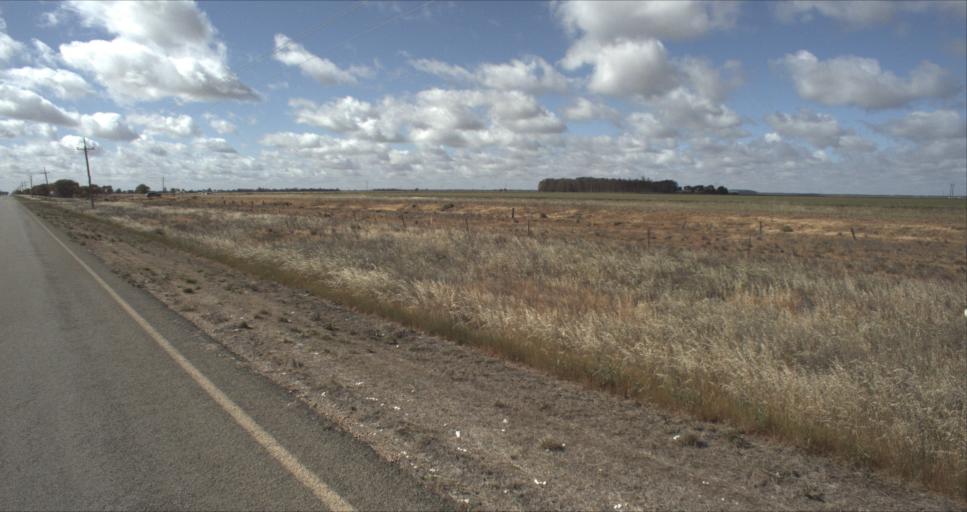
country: AU
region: New South Wales
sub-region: Leeton
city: Leeton
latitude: -34.5278
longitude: 146.2129
